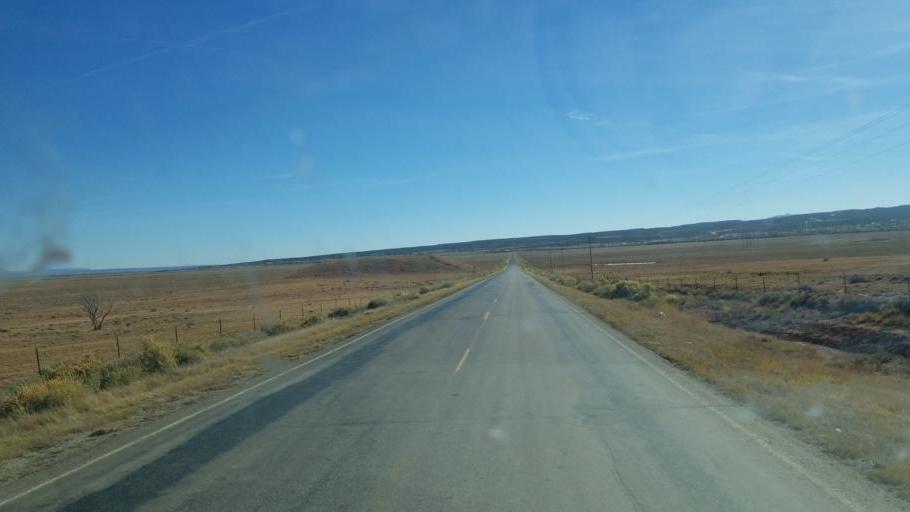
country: US
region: New Mexico
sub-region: McKinley County
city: Thoreau
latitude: 35.3903
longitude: -108.0491
